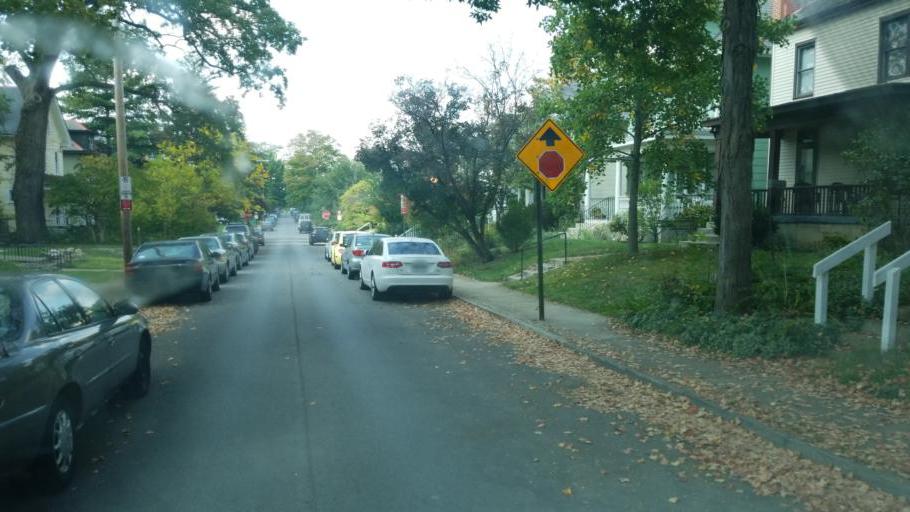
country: US
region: Ohio
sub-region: Franklin County
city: Grandview Heights
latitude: 40.0089
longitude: -83.0054
